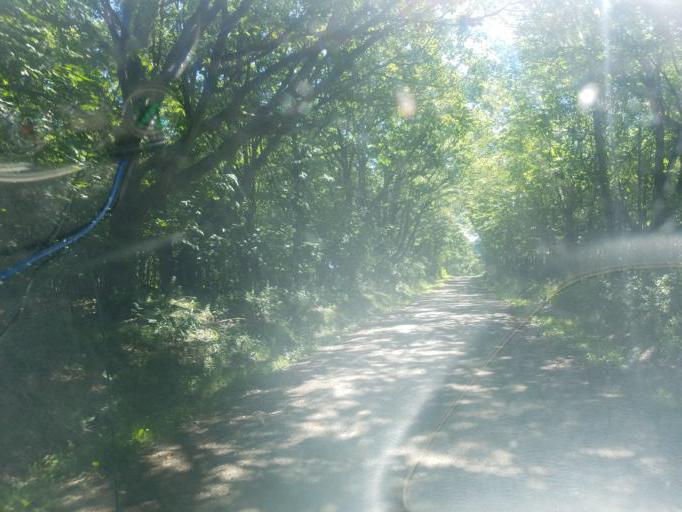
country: US
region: New York
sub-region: Ontario County
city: Naples
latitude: 42.6836
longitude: -77.3278
